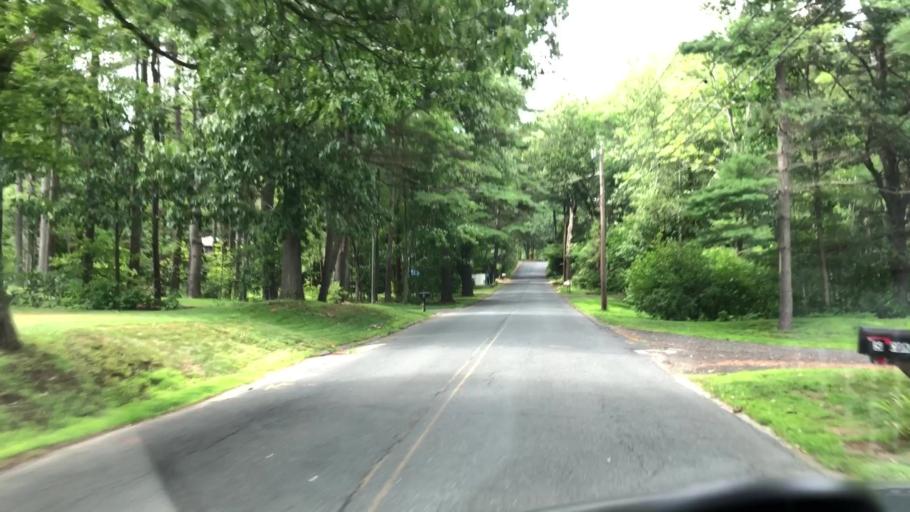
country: US
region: Massachusetts
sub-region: Hampshire County
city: Southampton
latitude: 42.2224
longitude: -72.6861
